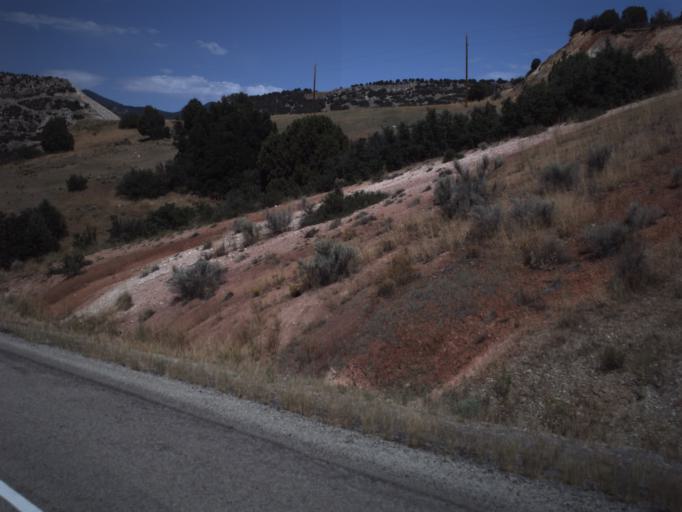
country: US
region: Utah
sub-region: Utah County
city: Mapleton
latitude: 39.9948
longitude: -111.4705
